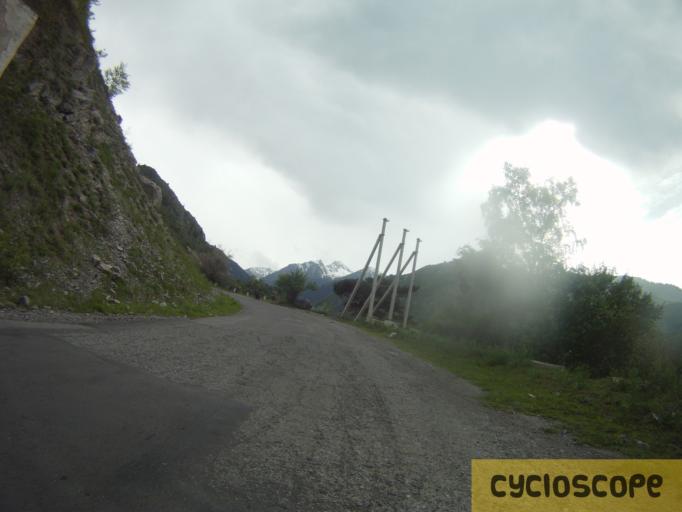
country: KZ
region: Almaty Oblysy
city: Esik
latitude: 43.2699
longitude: 77.4972
